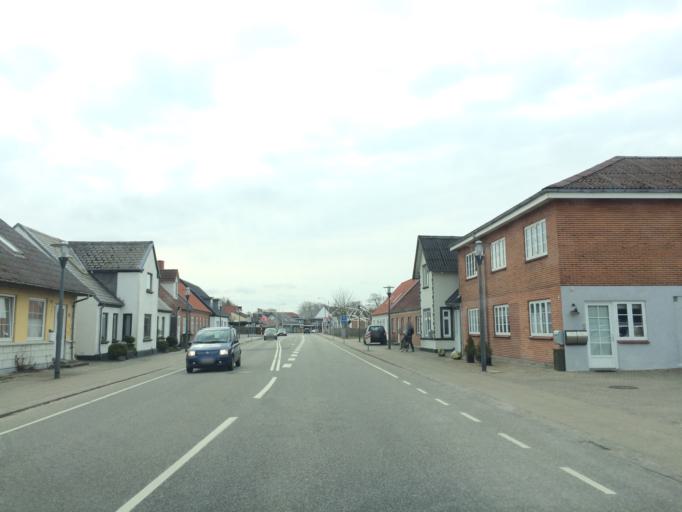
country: DK
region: Central Jutland
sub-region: Ringkobing-Skjern Kommune
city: Tarm
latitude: 55.9106
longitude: 8.5208
